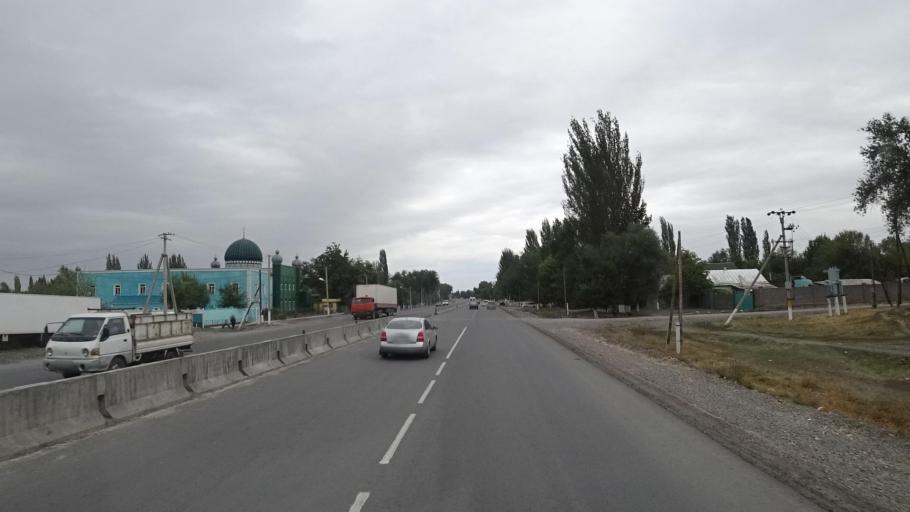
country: KG
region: Chuy
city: Kara-Balta
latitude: 42.8343
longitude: 73.9087
